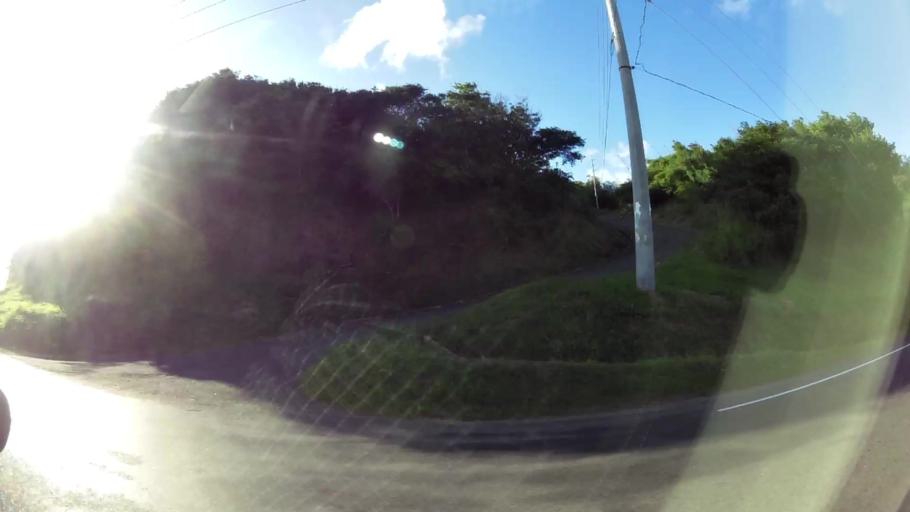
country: TT
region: Tobago
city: Scarborough
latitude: 11.1800
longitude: -60.7047
